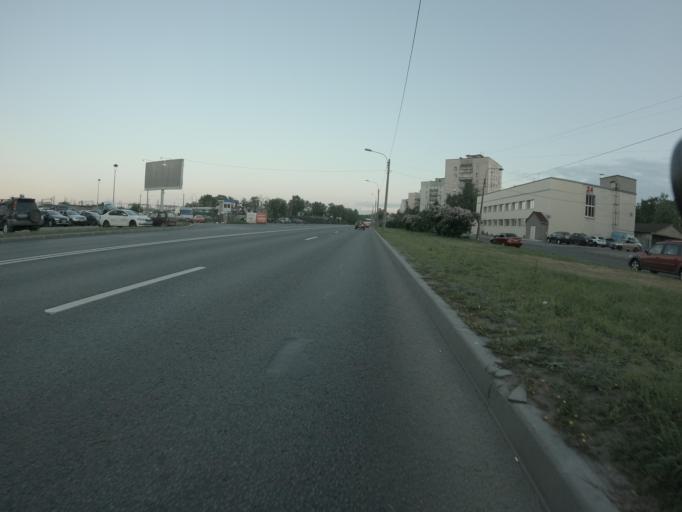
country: RU
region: St.-Petersburg
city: Dachnoye
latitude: 59.8491
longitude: 30.2805
